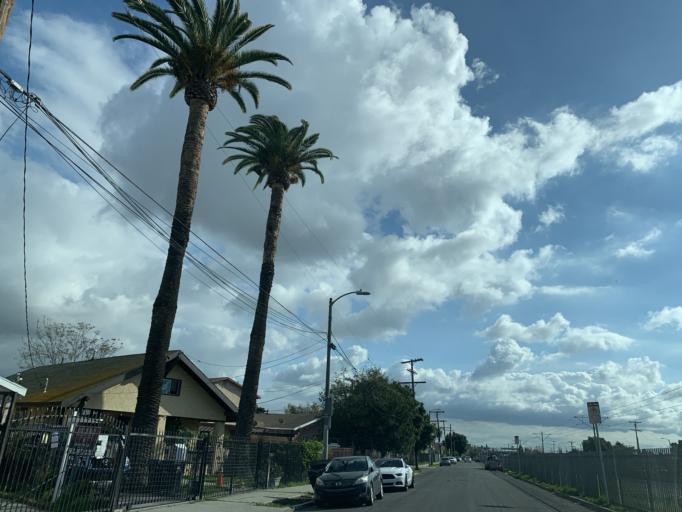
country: US
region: California
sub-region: Los Angeles County
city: Willowbrook
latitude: 33.9358
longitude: -118.2415
